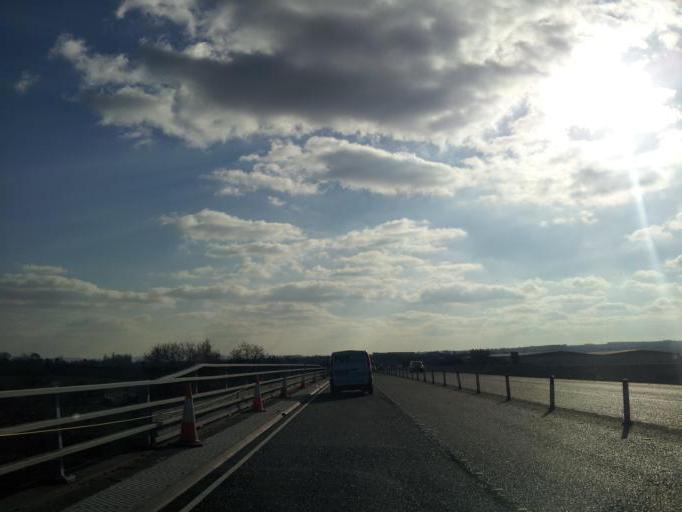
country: GB
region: England
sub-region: Somerset
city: Bridgwater
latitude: 51.1122
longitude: -2.9823
